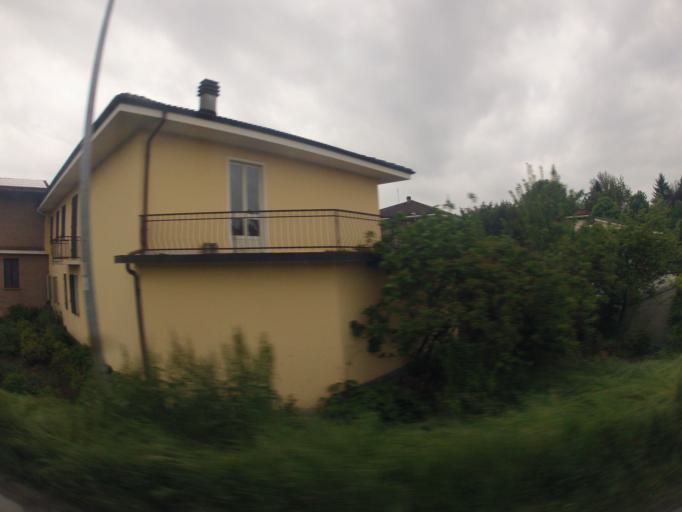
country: IT
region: Piedmont
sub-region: Provincia di Cuneo
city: Casalgrasso
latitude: 44.8211
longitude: 7.6236
